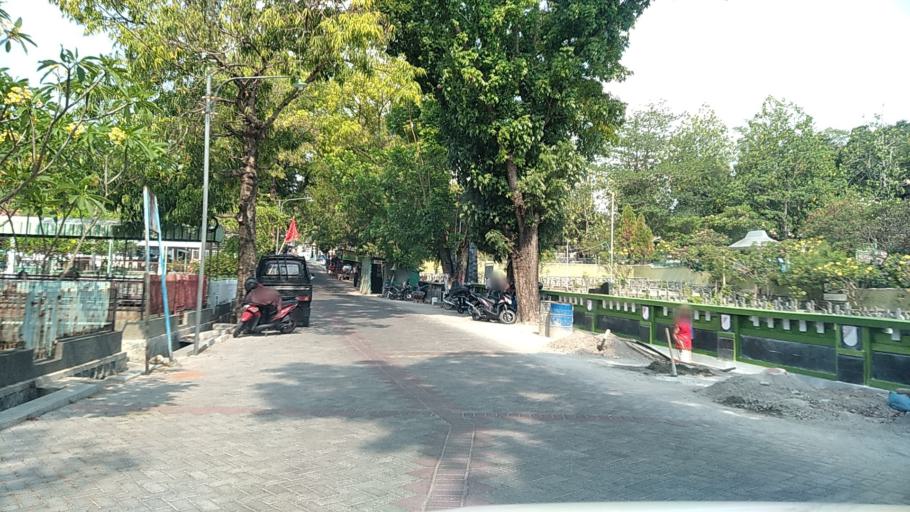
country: ID
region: Central Java
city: Semarang
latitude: -6.9914
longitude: 110.4114
